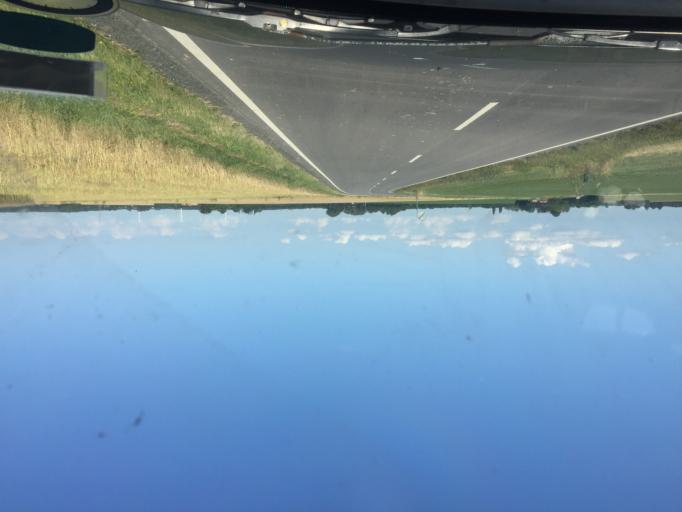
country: DK
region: Zealand
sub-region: Lolland Kommune
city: Maribo
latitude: 54.7968
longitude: 11.5523
